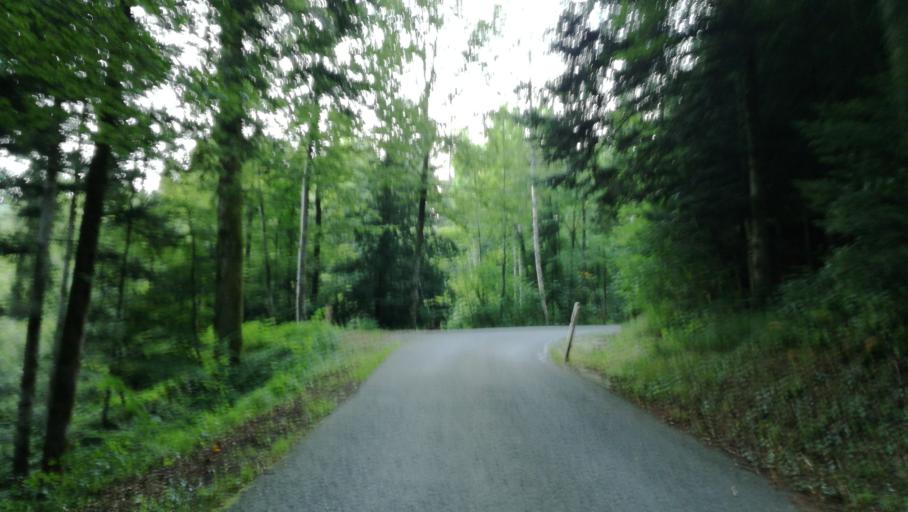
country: CH
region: Zug
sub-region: Zug
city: Unterageri
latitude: 47.1518
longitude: 8.5560
